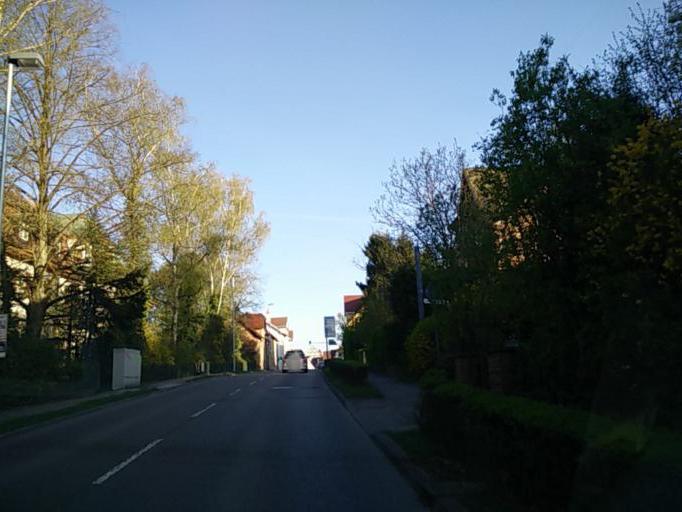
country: DE
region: Baden-Wuerttemberg
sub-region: Regierungsbezirk Stuttgart
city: Herrenberg
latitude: 48.5933
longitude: 8.8750
